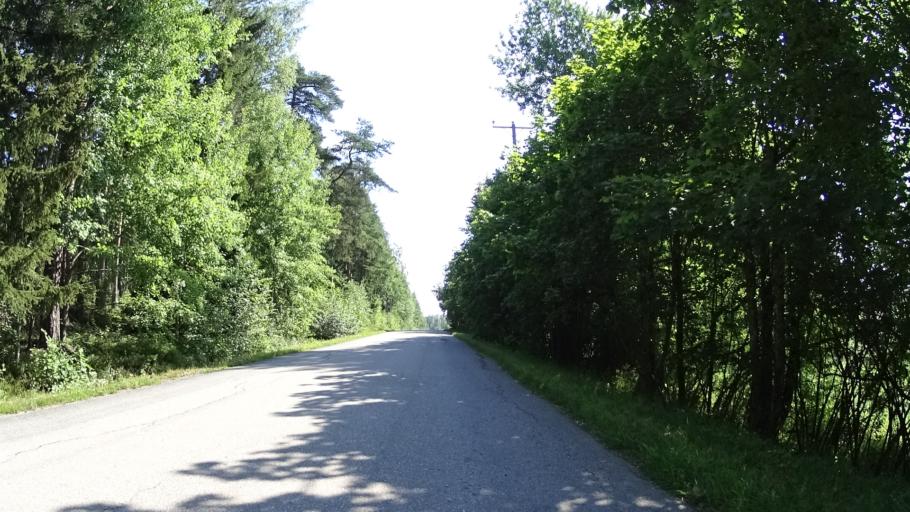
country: FI
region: Uusimaa
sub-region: Helsinki
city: Jaervenpaeae
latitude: 60.4470
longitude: 25.0878
